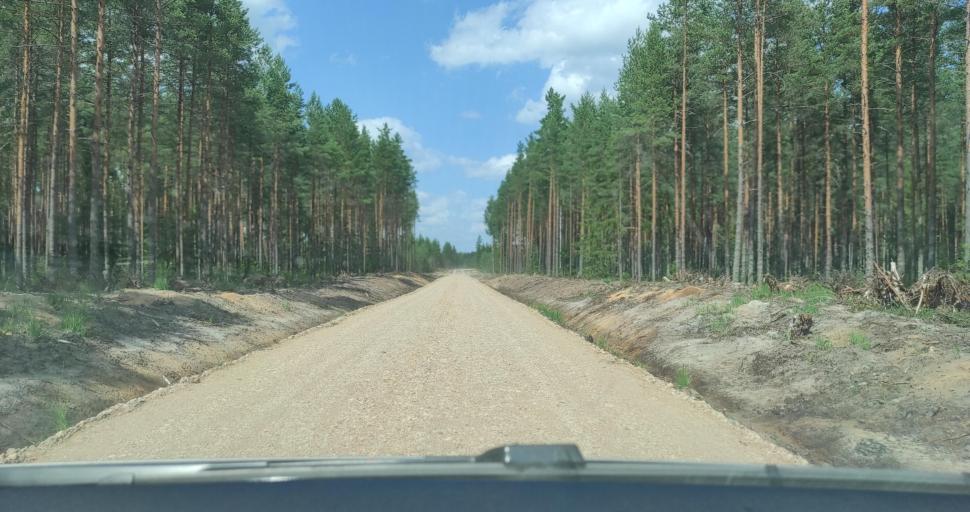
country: LV
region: Kuldigas Rajons
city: Kuldiga
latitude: 57.0556
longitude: 22.1902
